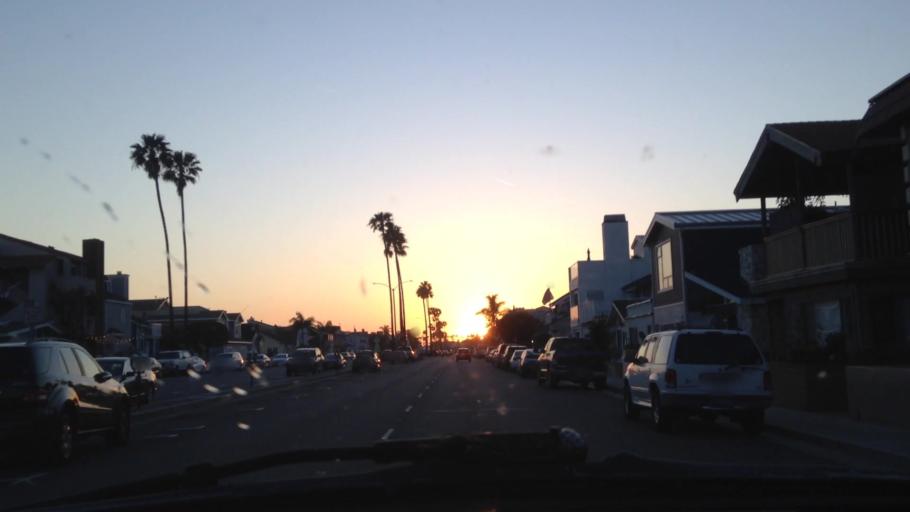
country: US
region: California
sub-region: Orange County
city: Newport Beach
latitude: 33.6051
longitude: -117.9120
